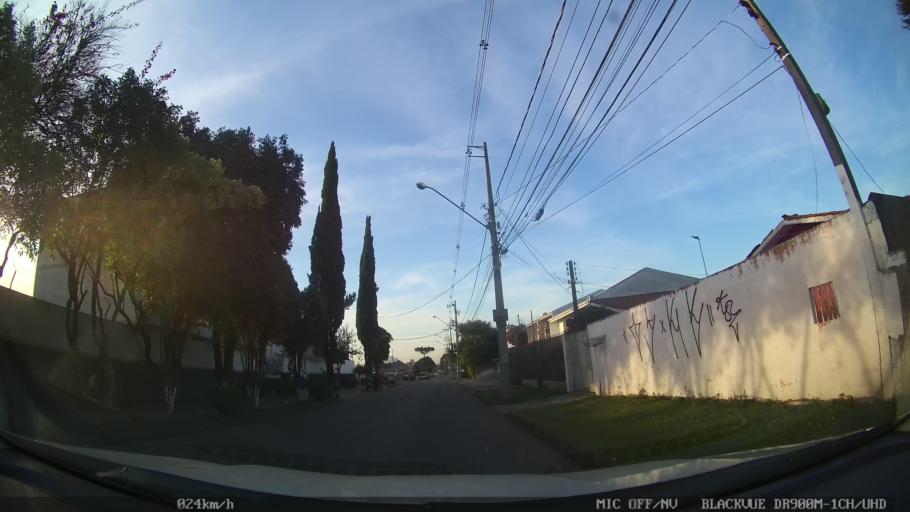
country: BR
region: Parana
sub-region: Pinhais
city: Pinhais
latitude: -25.4477
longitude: -49.1743
